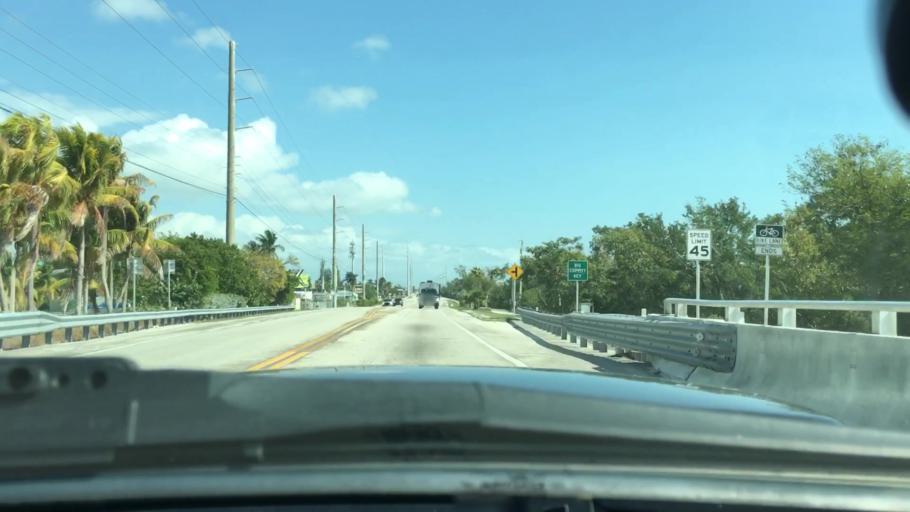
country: US
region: Florida
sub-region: Monroe County
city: Big Coppitt Key
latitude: 24.5932
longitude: -81.6653
